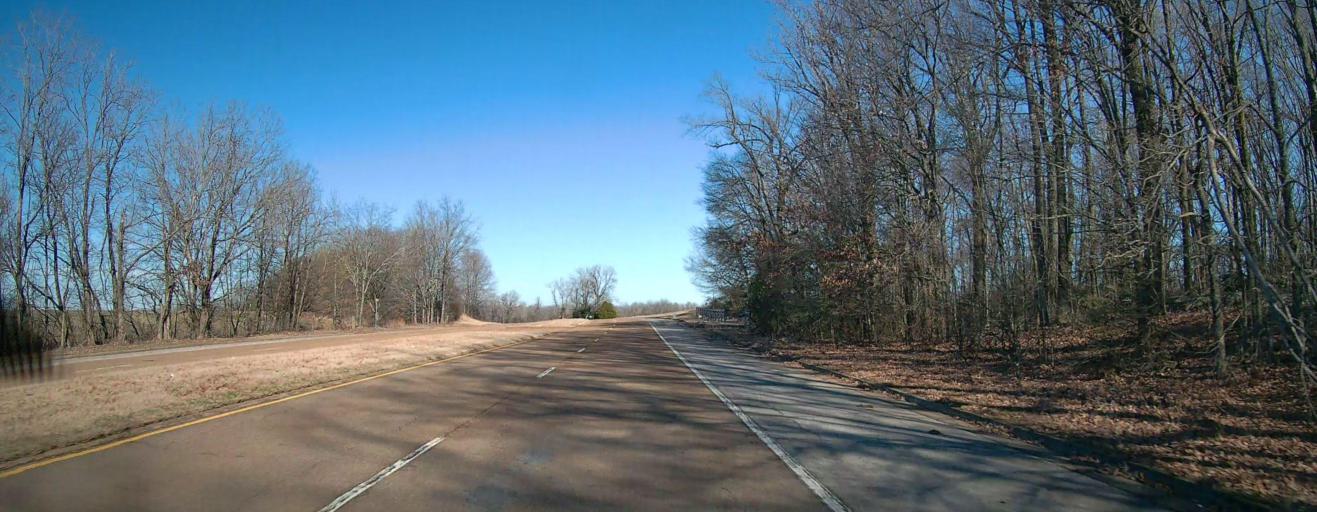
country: US
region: Tennessee
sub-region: Shelby County
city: Bartlett
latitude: 35.2566
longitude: -89.8916
